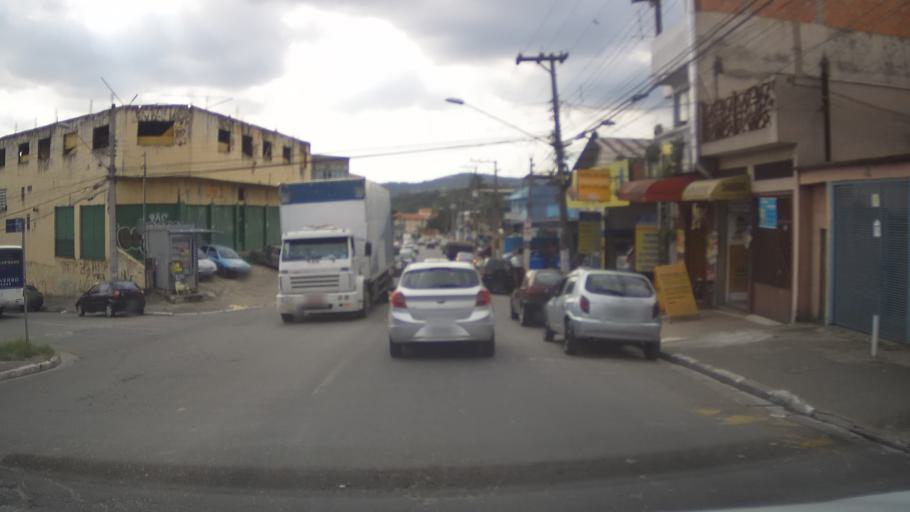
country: BR
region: Sao Paulo
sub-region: Guarulhos
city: Guarulhos
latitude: -23.4151
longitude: -46.4601
